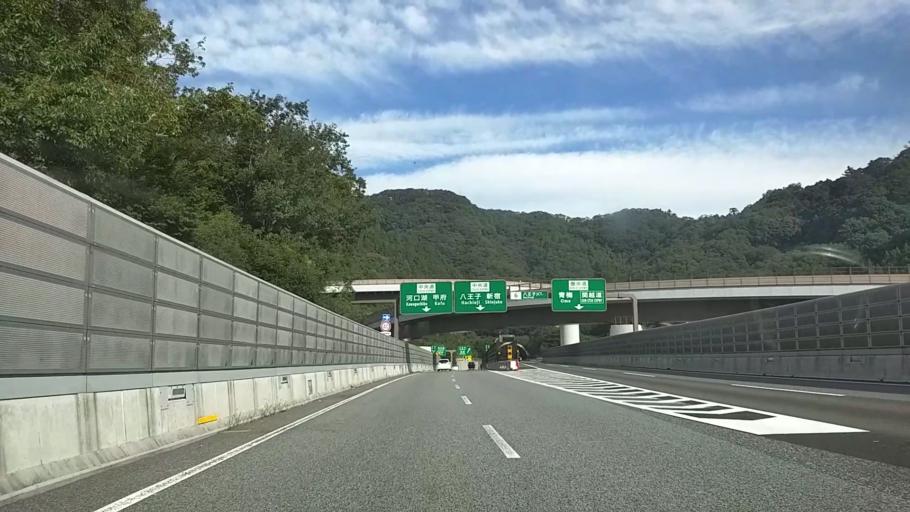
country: JP
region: Tokyo
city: Hachioji
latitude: 35.6391
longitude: 139.2554
